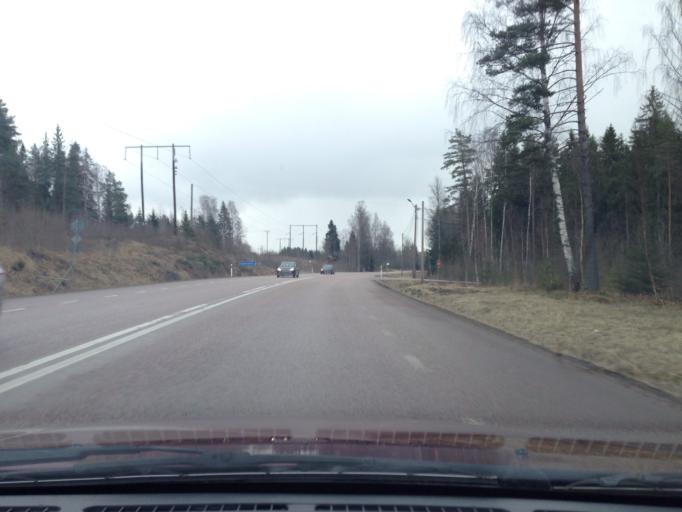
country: SE
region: Dalarna
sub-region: Ludvika Kommun
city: Ludvika
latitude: 60.1546
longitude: 15.2557
